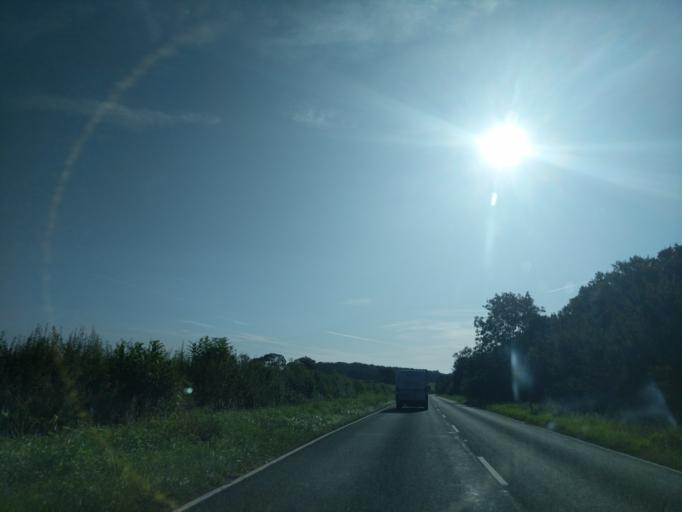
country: GB
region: England
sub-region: District of Rutland
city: Clipsham
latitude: 52.8033
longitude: -0.5864
